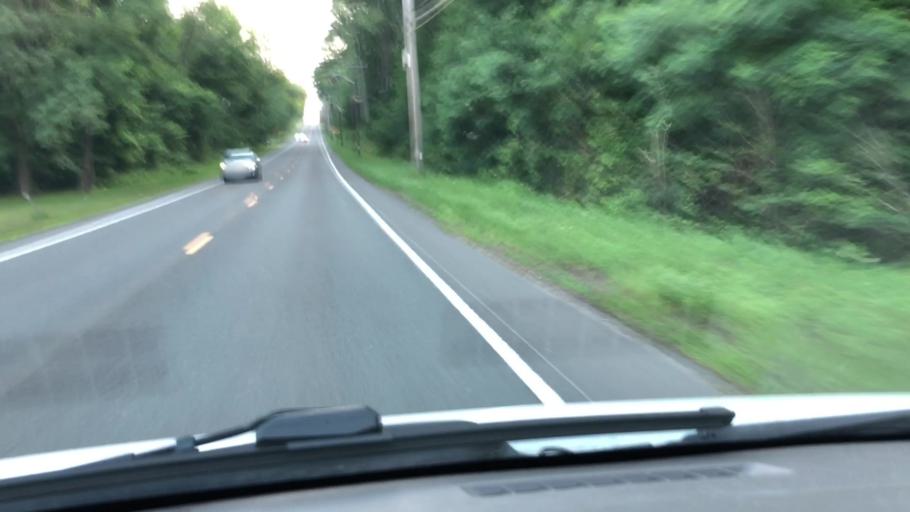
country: US
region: Massachusetts
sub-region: Hampshire County
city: Williamsburg
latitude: 42.3537
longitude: -72.6911
